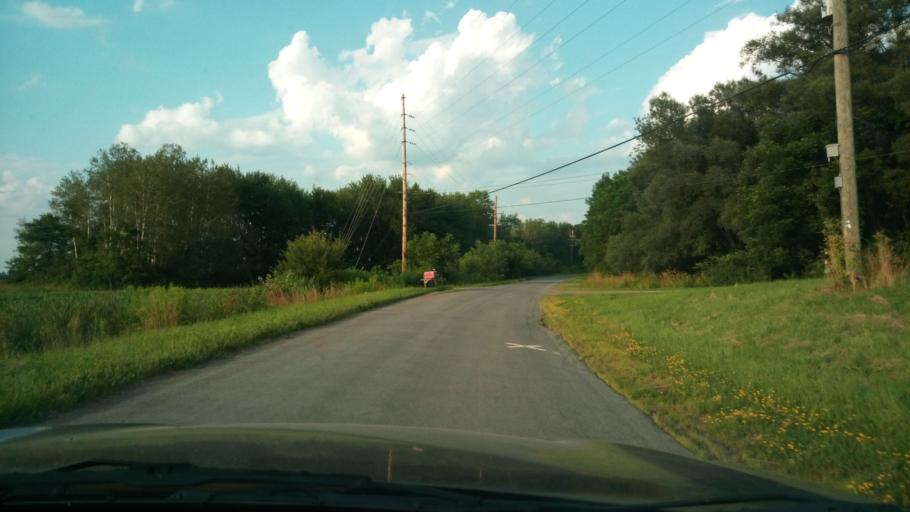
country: US
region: New York
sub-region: Wayne County
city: Clyde
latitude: 43.0867
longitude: -76.9124
